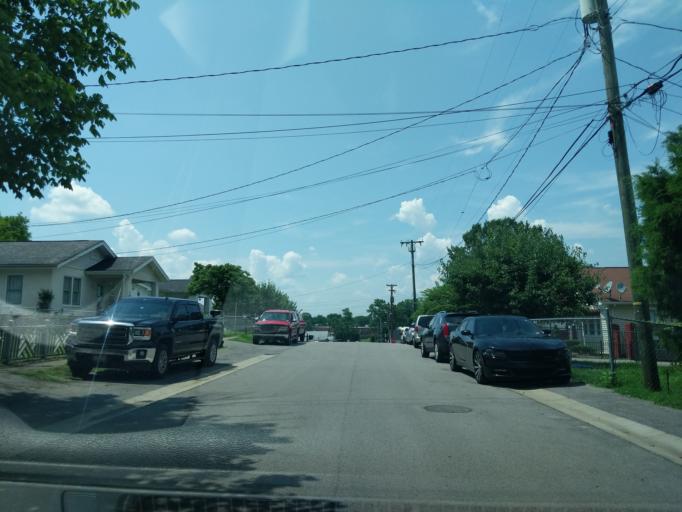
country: US
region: Tennessee
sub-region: Davidson County
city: Lakewood
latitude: 36.2479
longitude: -86.6396
